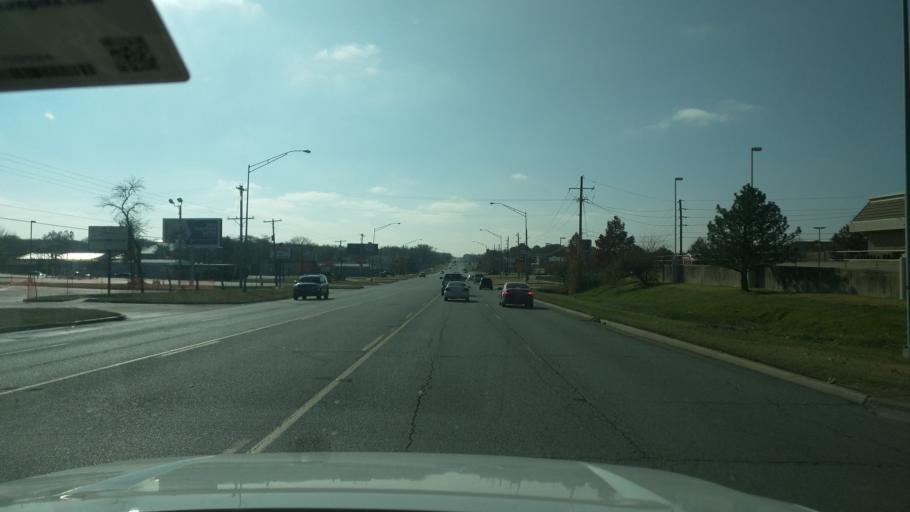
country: US
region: Oklahoma
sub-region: Washington County
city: Bartlesville
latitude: 36.7127
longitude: -95.9352
